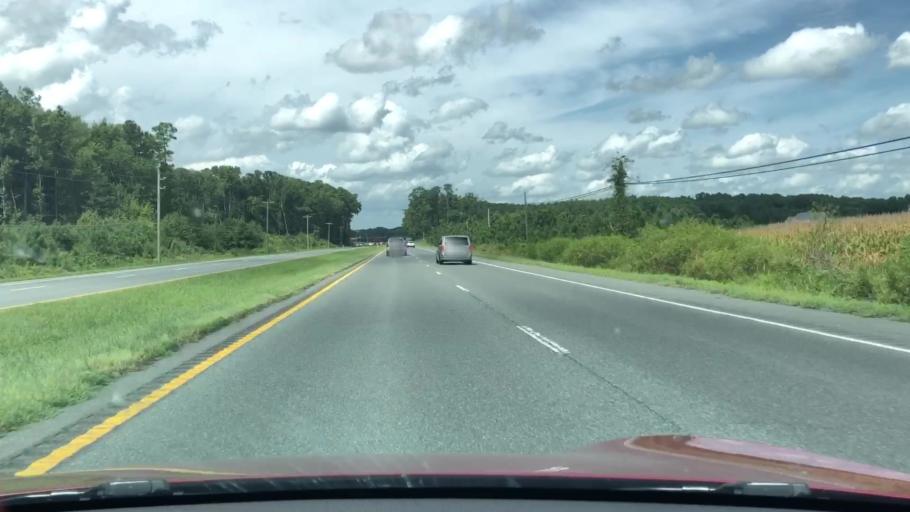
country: US
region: Virginia
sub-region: Accomack County
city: Wattsville
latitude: 37.9153
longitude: -75.5491
